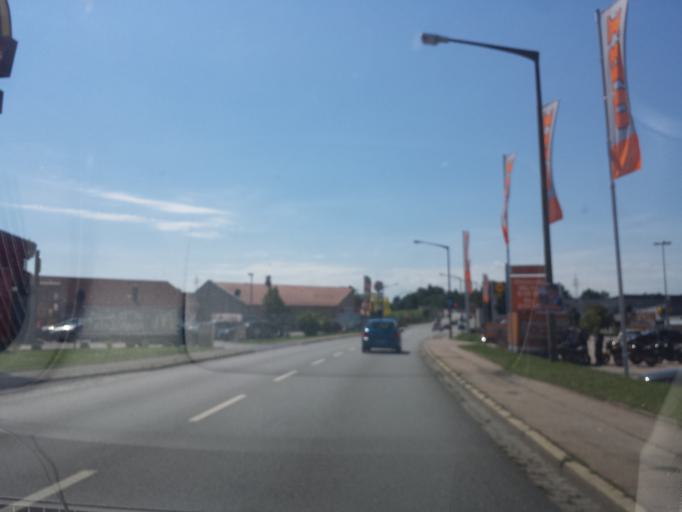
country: DE
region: Bavaria
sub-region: Upper Palatinate
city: Cham
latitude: 49.2030
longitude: 12.6640
